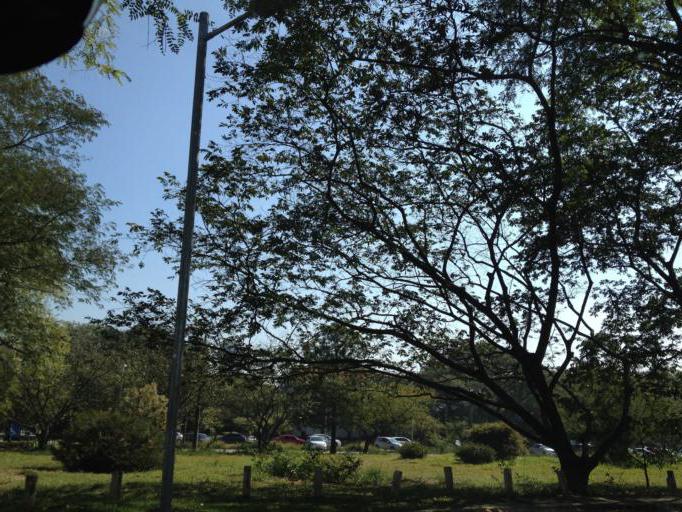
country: BR
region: Sao Paulo
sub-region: Osasco
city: Osasco
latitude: -23.5582
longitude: -46.7313
